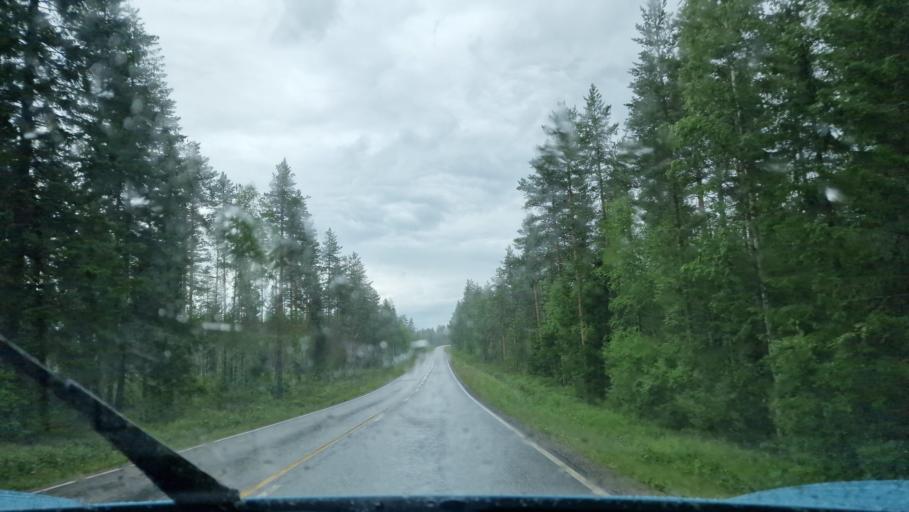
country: FI
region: Central Finland
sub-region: Saarijaervi-Viitasaari
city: Pylkoenmaeki
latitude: 62.5947
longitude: 24.5898
